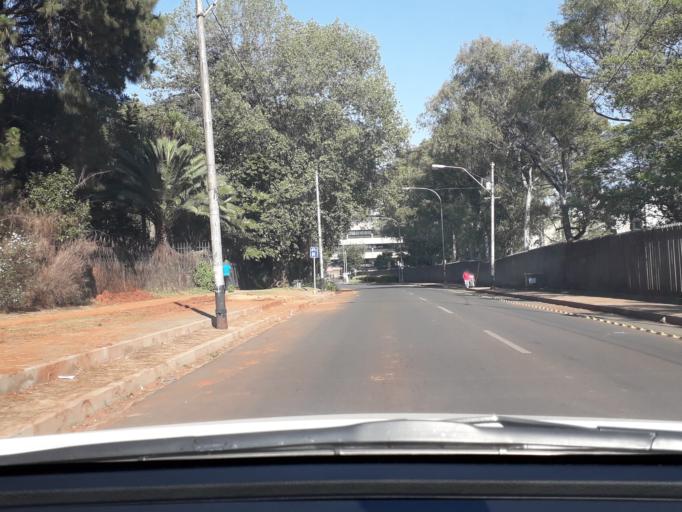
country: ZA
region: Gauteng
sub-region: City of Johannesburg Metropolitan Municipality
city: Johannesburg
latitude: -26.1859
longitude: 28.0003
